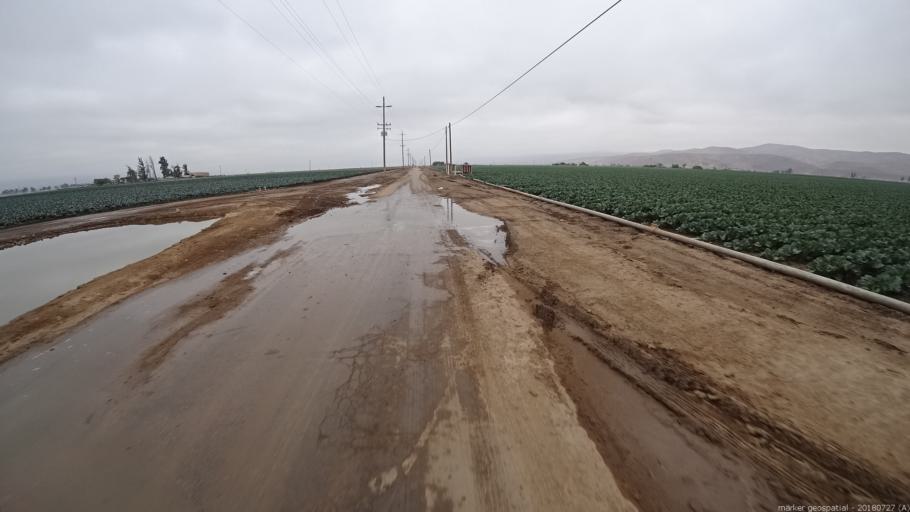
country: US
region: California
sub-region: Monterey County
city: Greenfield
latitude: 36.3363
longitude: -121.2322
